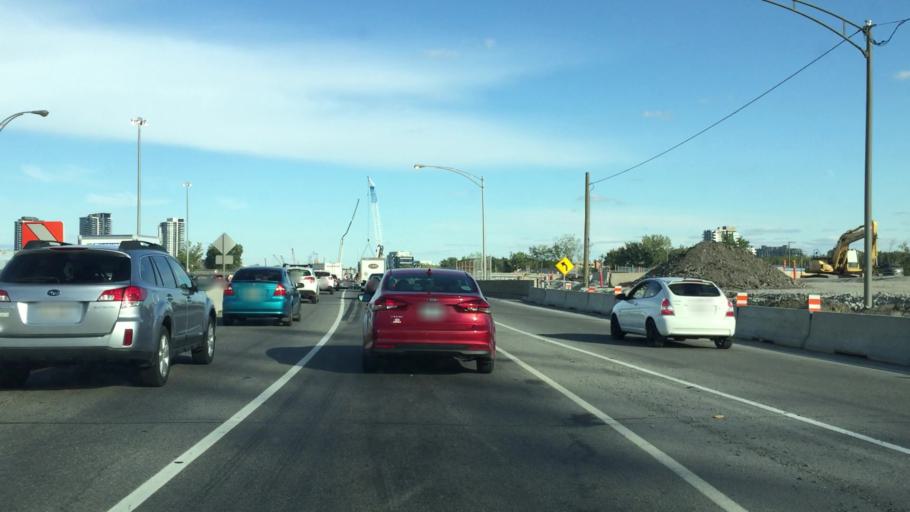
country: CA
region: Quebec
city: Westmount
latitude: 45.4717
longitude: -73.5582
